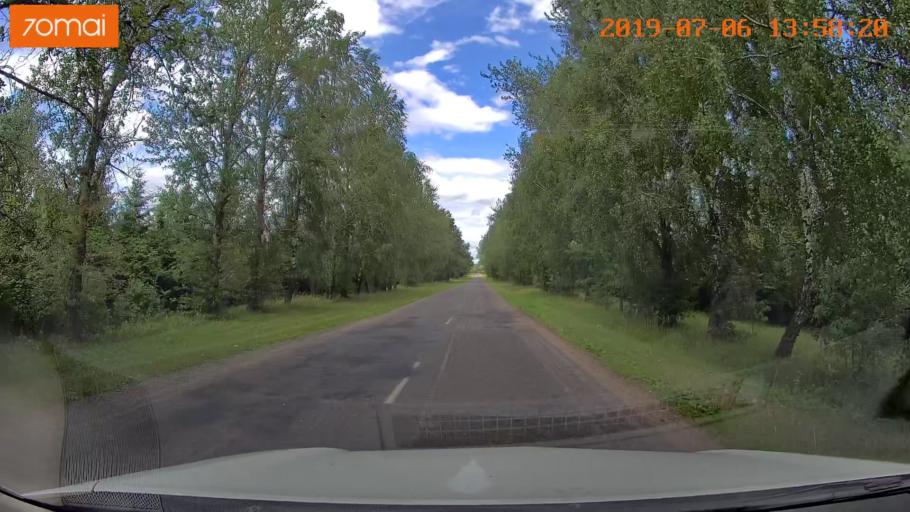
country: BY
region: Minsk
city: Ivyanyets
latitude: 53.7828
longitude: 26.8087
